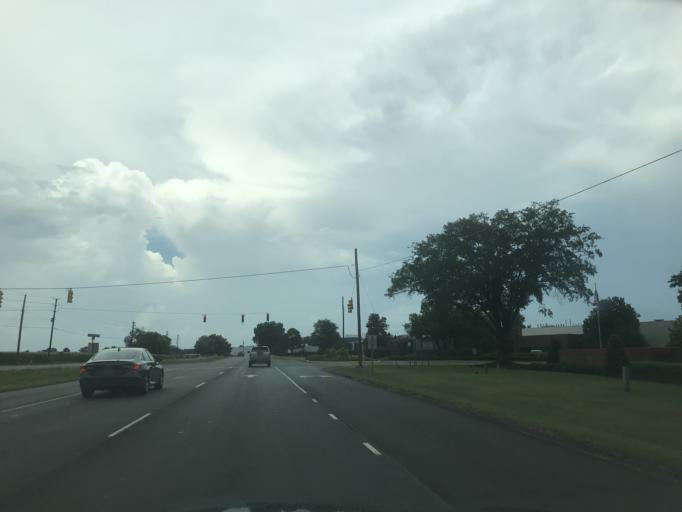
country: US
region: North Carolina
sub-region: Johnston County
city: Clayton
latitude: 35.6185
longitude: -78.4201
